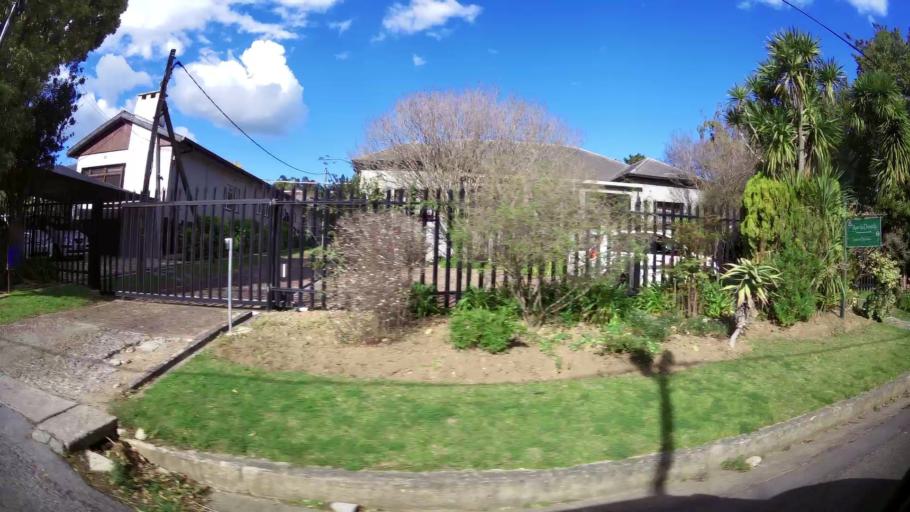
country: ZA
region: Western Cape
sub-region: Overberg District Municipality
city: Swellendam
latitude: -34.0200
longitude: 20.4519
